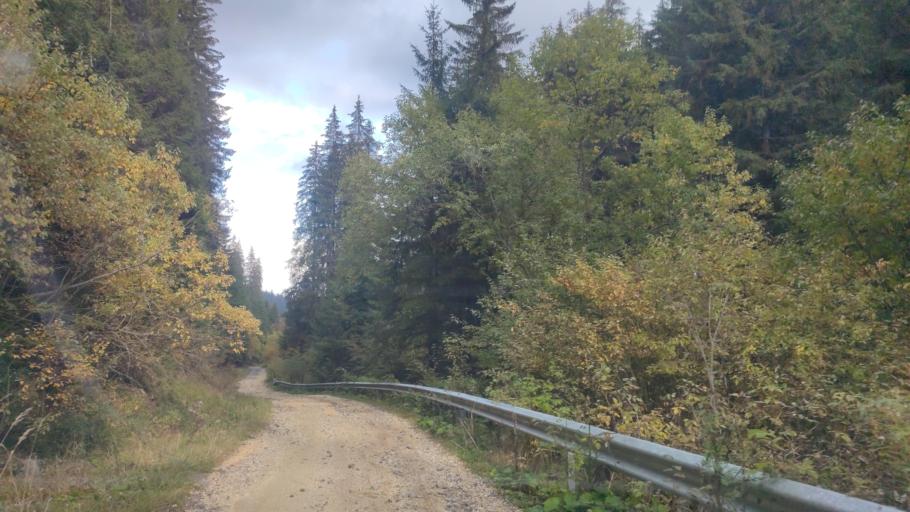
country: RO
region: Harghita
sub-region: Comuna Madaras
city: Madaras
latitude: 46.4681
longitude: 25.6243
